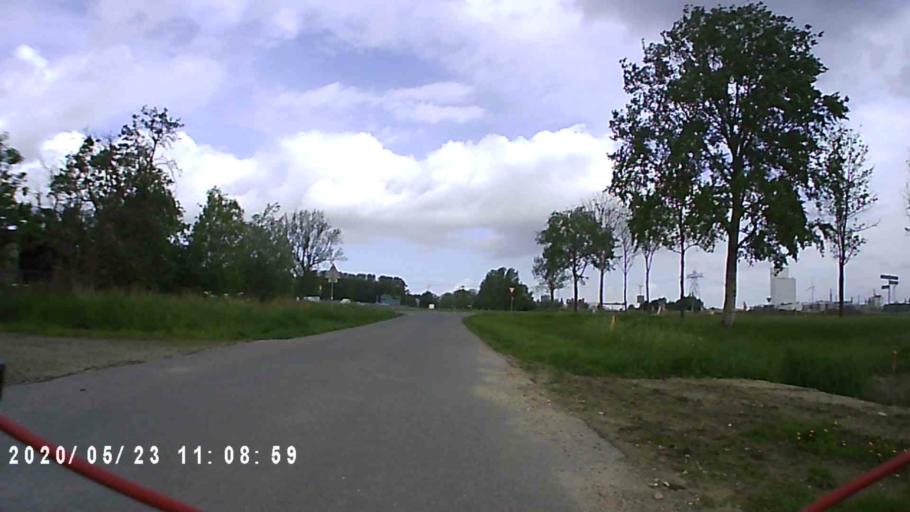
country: NL
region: Groningen
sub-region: Gemeente Delfzijl
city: Delfzijl
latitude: 53.3042
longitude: 6.9547
